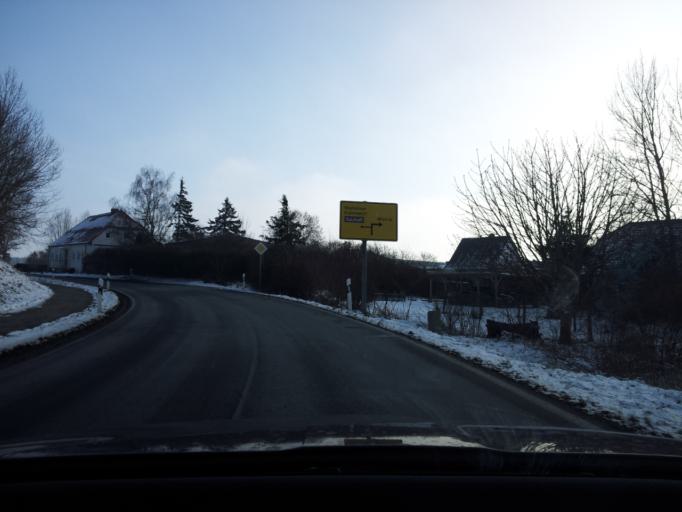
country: DE
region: Mecklenburg-Vorpommern
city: Blowatz
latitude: 53.9627
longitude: 11.4878
